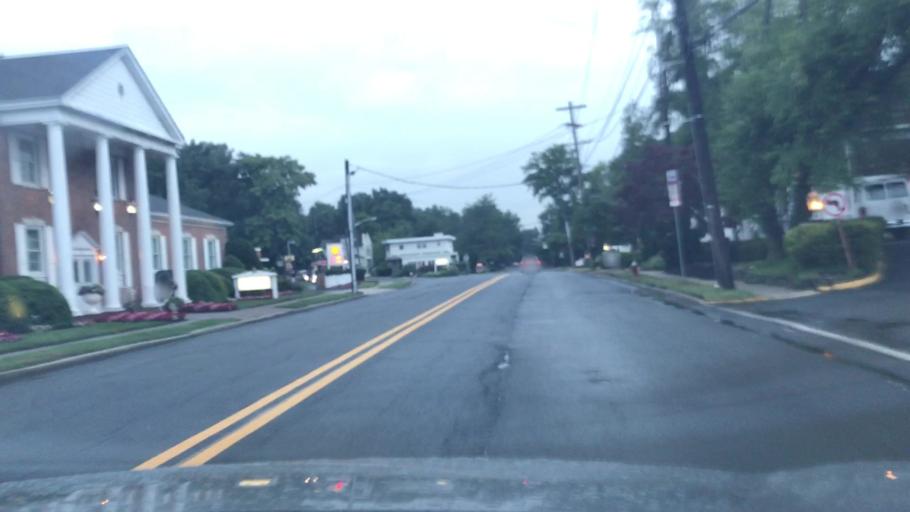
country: US
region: New Jersey
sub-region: Bergen County
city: Tenafly
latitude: 40.9229
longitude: -73.9642
